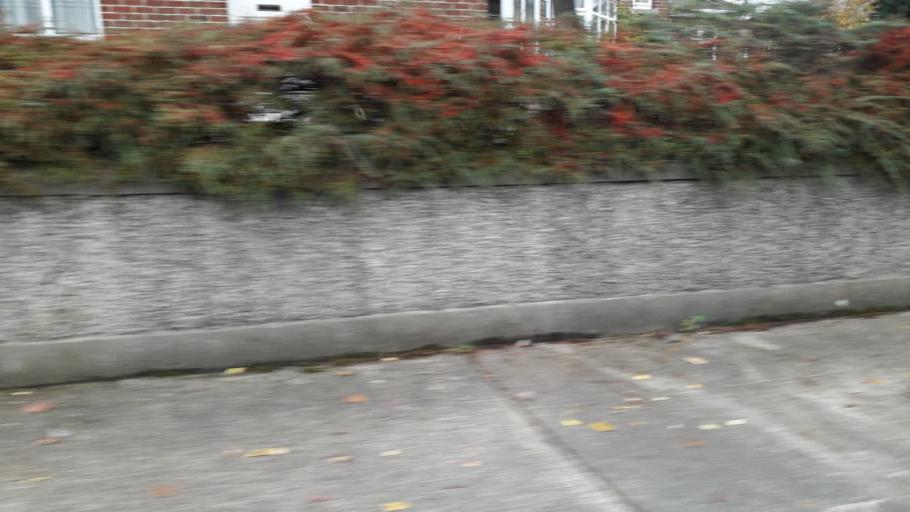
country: IE
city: Milltown
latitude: 53.3123
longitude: -6.2417
